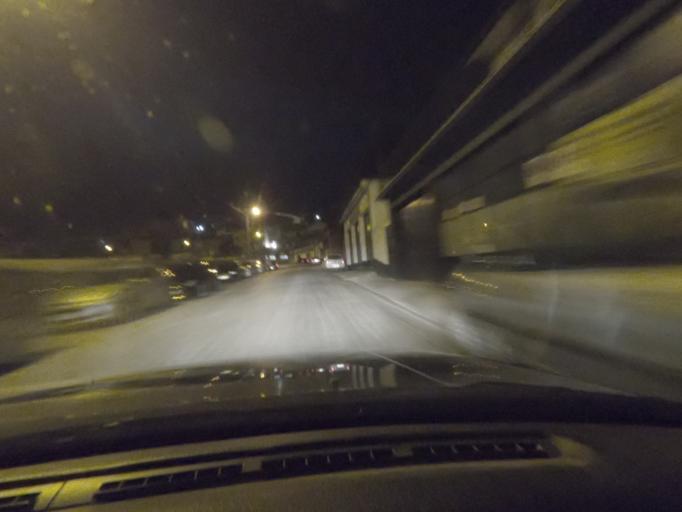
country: PT
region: Vila Real
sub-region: Peso da Regua
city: Peso da Regua
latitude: 41.1655
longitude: -7.7824
